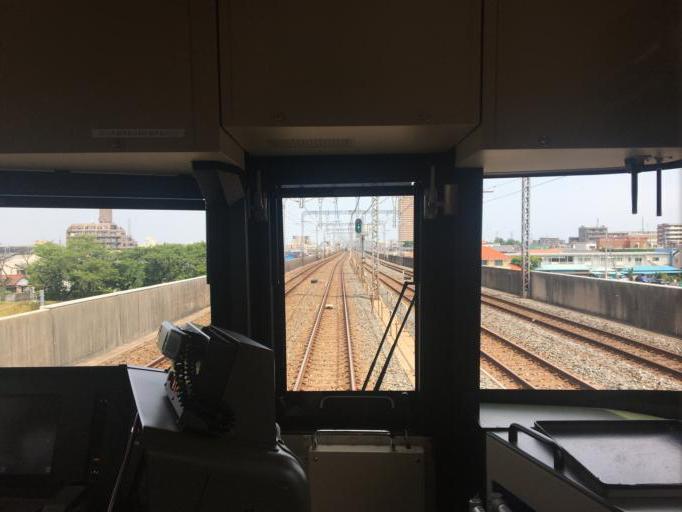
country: JP
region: Saitama
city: Koshigaya
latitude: 35.8947
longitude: 139.7829
